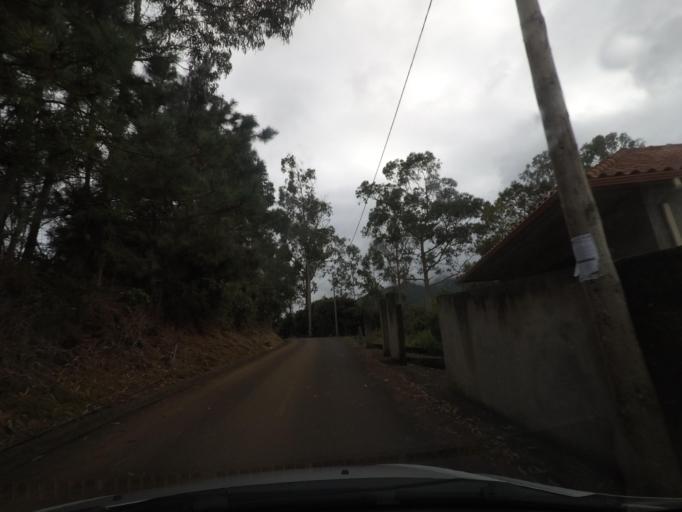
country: PT
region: Madeira
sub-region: Santana
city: Santana
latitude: 32.7821
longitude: -16.8776
